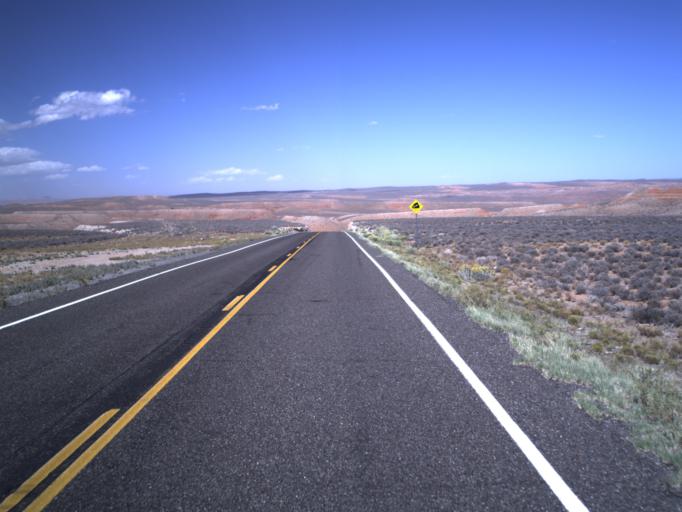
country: US
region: Utah
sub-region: Wayne County
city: Loa
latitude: 38.1245
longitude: -110.6179
